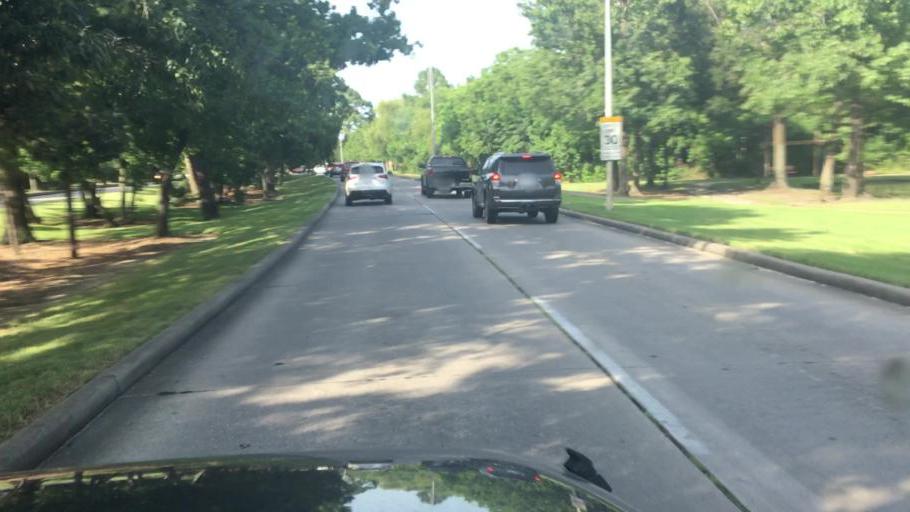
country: US
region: Texas
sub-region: Harris County
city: Atascocita
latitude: 29.9268
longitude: -95.1792
